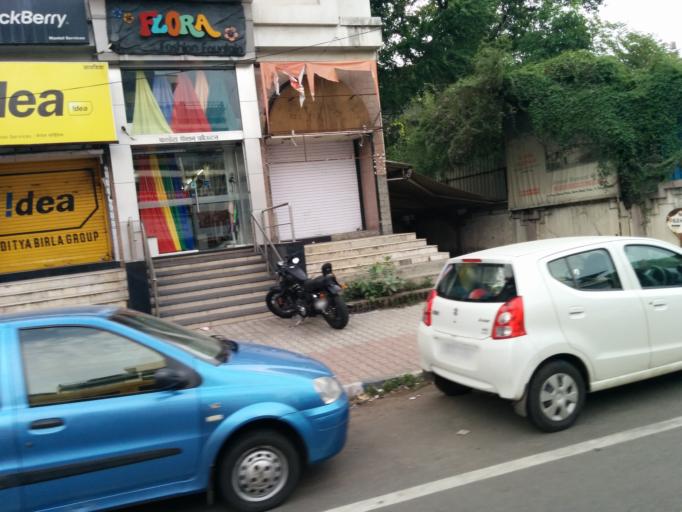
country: IN
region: Maharashtra
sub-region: Pune Division
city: Pune
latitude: 18.5105
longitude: 73.8345
